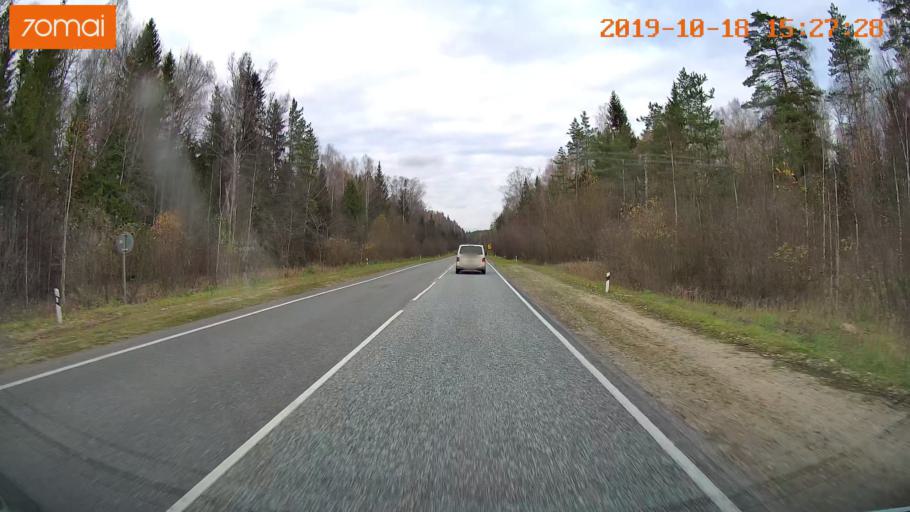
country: RU
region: Vladimir
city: Anopino
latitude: 55.7536
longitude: 40.6711
